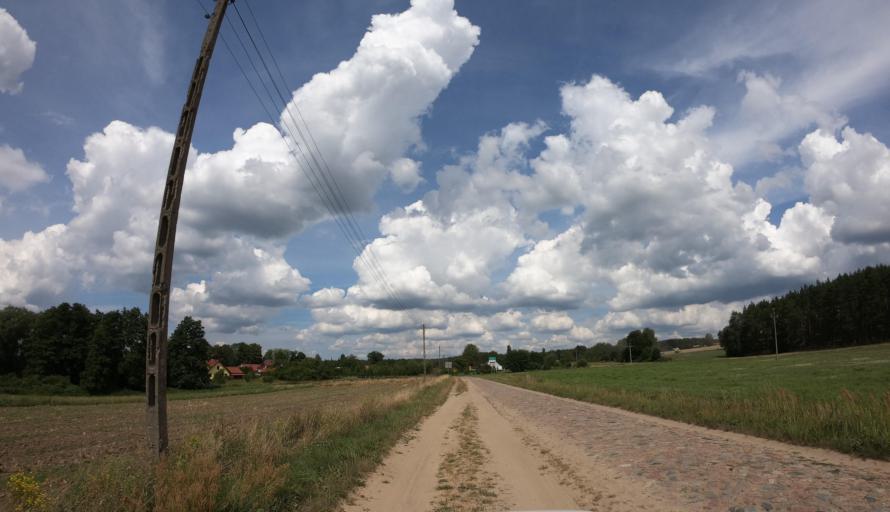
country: PL
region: West Pomeranian Voivodeship
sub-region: Powiat stargardzki
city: Kobylanka
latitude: 53.3204
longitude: 14.8257
